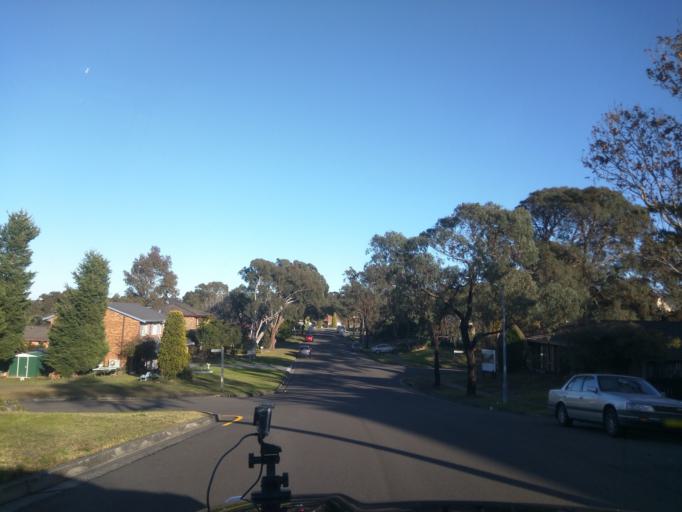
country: AU
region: New South Wales
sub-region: Sutherland Shire
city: Menai
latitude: -34.0204
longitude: 151.0248
